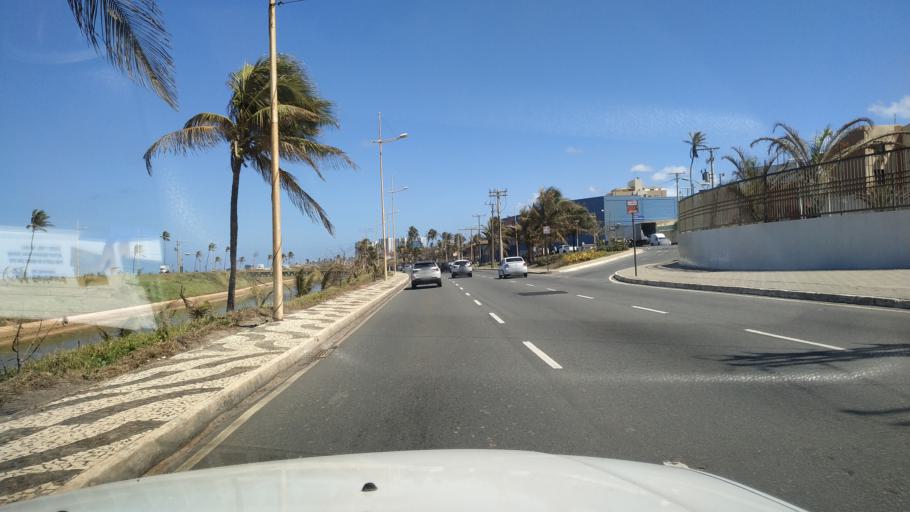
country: BR
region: Bahia
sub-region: Lauro De Freitas
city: Lauro de Freitas
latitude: -12.9591
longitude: -38.3947
